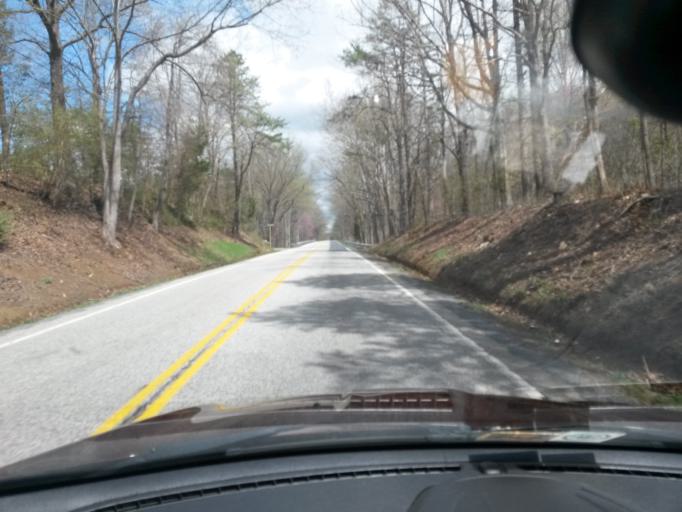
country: US
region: Virginia
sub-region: City of Buena Vista
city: Buena Vista
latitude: 37.6855
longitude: -79.4007
